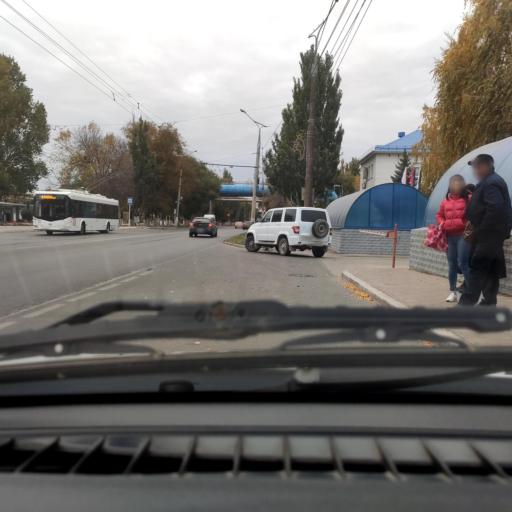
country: RU
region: Samara
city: Tol'yatti
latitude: 53.5551
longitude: 49.4513
